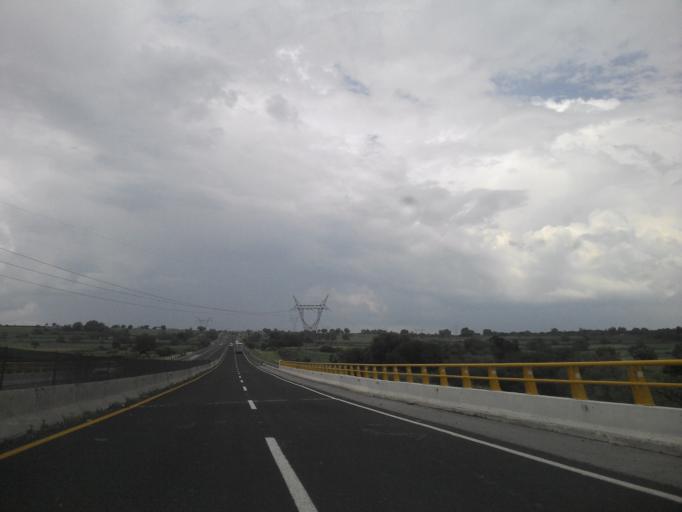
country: MX
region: Hidalgo
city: San Marcos
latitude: 20.0770
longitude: -99.3484
